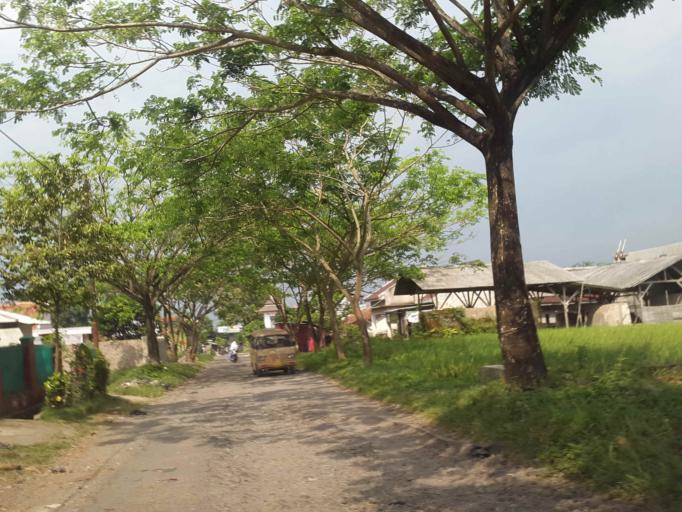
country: ID
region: West Java
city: Ciranjang-hilir
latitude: -6.7174
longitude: 107.2385
